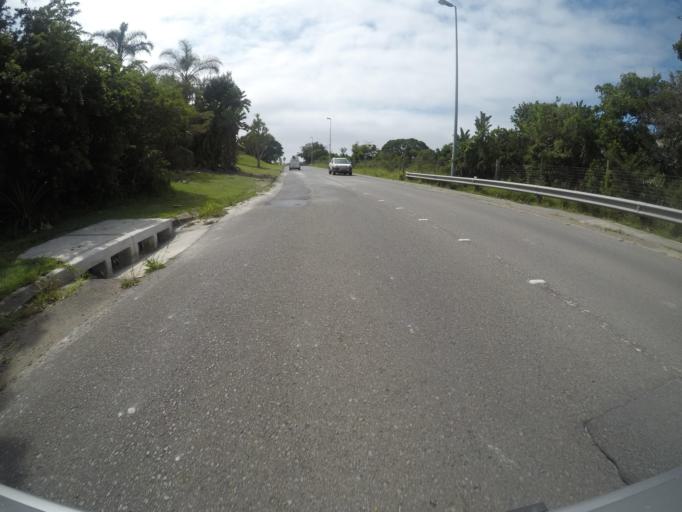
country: ZA
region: Eastern Cape
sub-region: Buffalo City Metropolitan Municipality
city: East London
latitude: -32.9809
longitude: 27.9340
